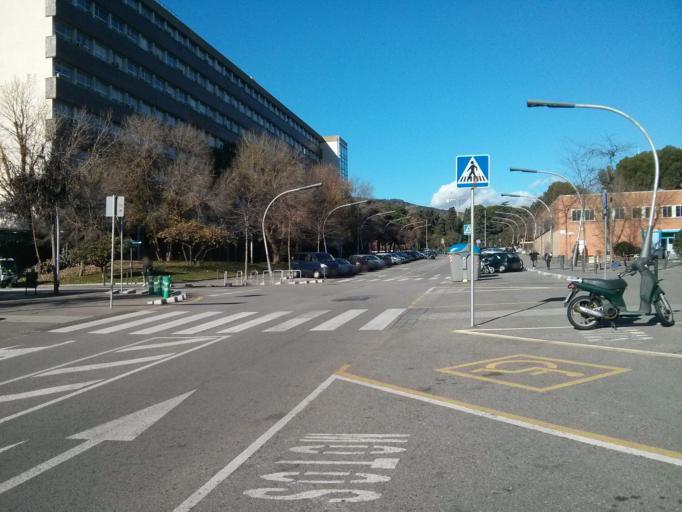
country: ES
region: Catalonia
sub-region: Provincia de Barcelona
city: les Corts
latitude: 41.3842
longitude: 2.1189
